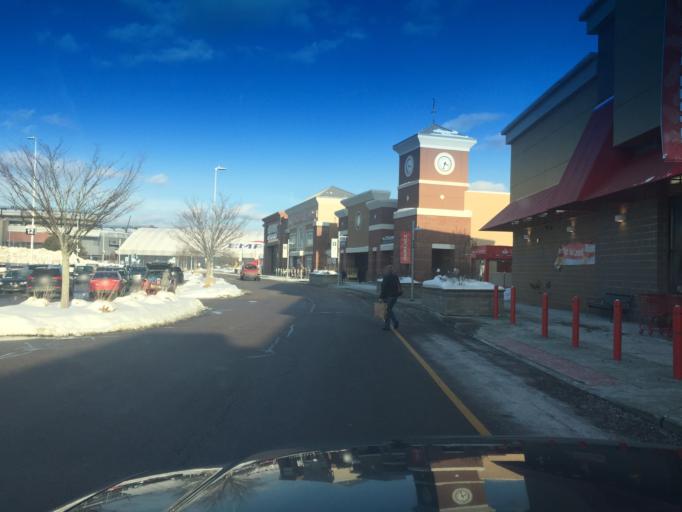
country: US
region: Massachusetts
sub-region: Norfolk County
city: Foxborough
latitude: 42.0867
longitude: -71.2696
